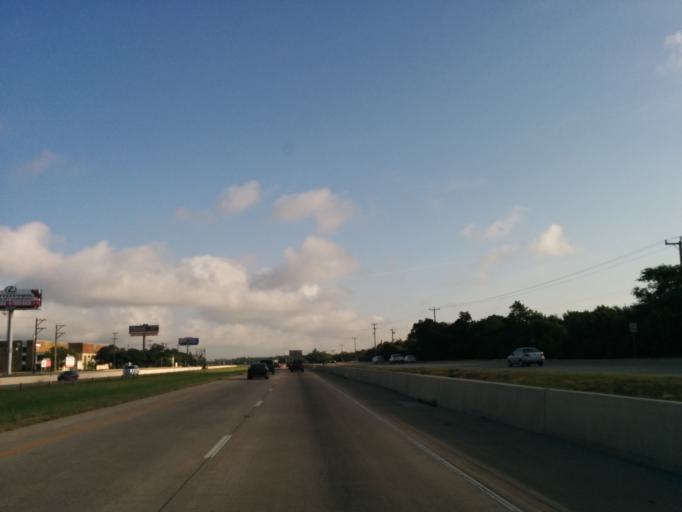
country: US
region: Texas
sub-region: Bexar County
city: Cross Mountain
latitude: 29.6308
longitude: -98.6118
